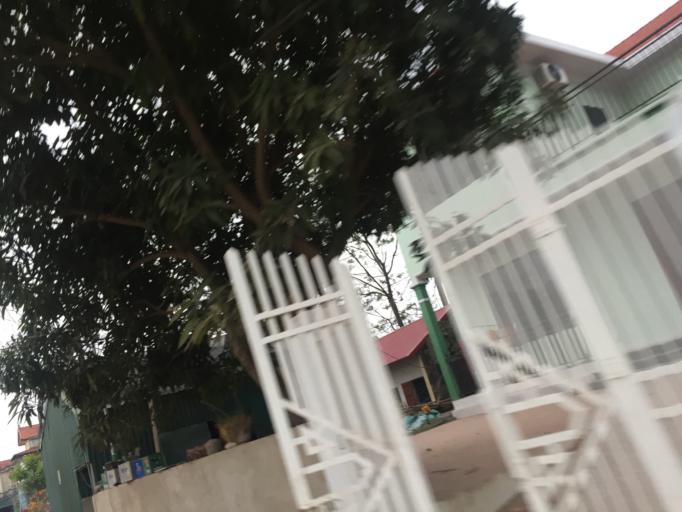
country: VN
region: Hung Yen
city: Van Giang
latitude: 20.9689
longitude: 105.9161
